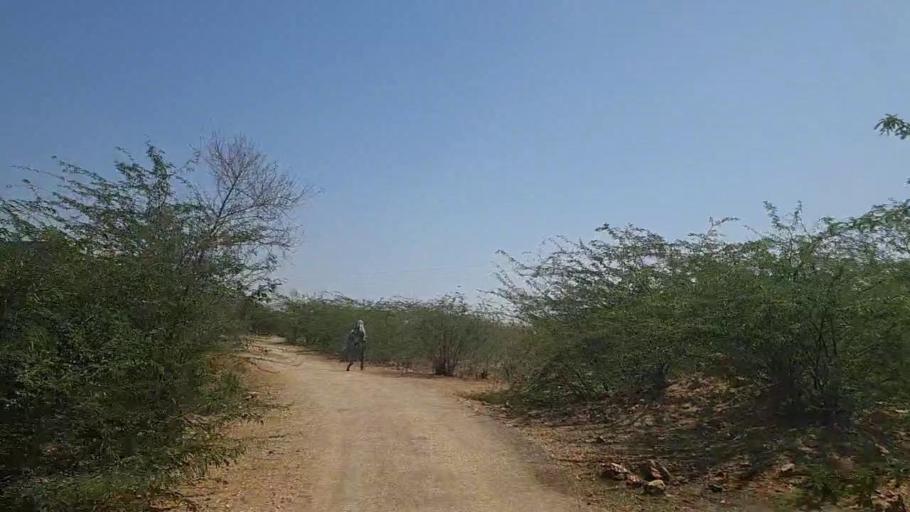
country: PK
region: Sindh
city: Thatta
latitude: 24.8409
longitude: 68.0087
